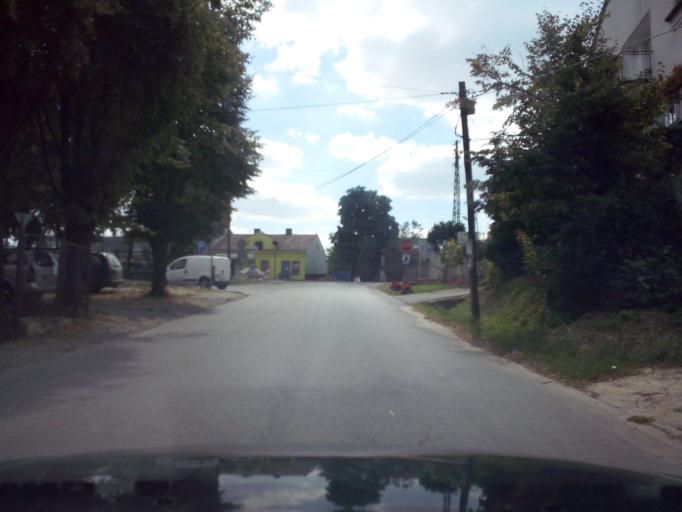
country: PL
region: Swietokrzyskie
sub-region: Powiat staszowski
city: Staszow
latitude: 50.5910
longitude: 21.1010
